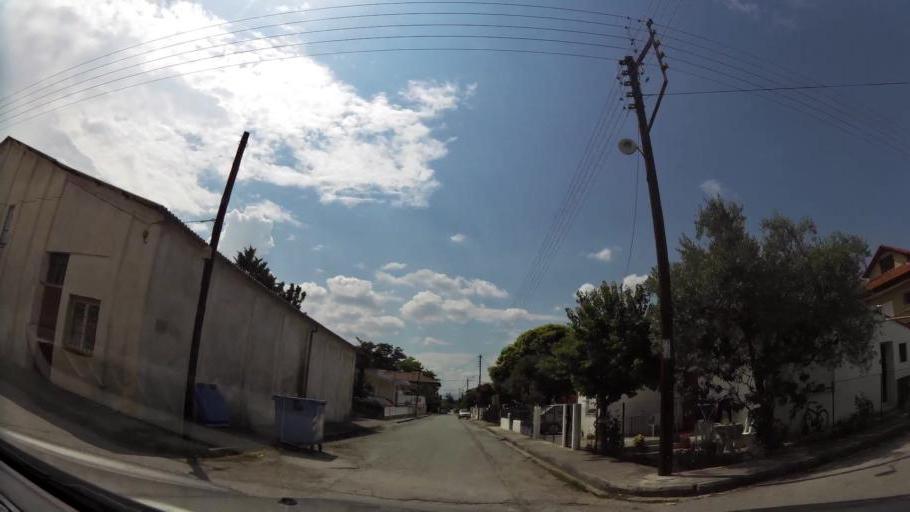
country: GR
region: Central Macedonia
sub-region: Nomos Pierias
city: Korinos
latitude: 40.3168
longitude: 22.5839
